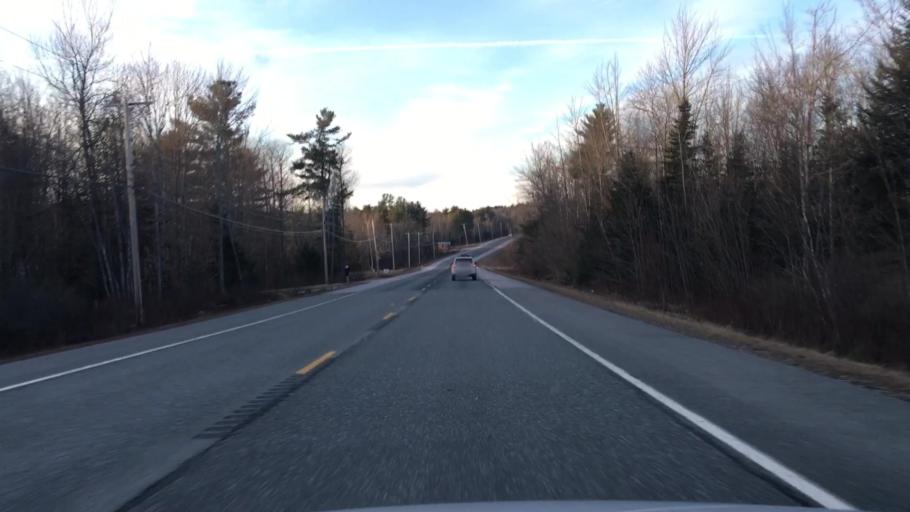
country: US
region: Maine
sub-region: Hancock County
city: Dedham
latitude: 44.6315
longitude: -68.5421
